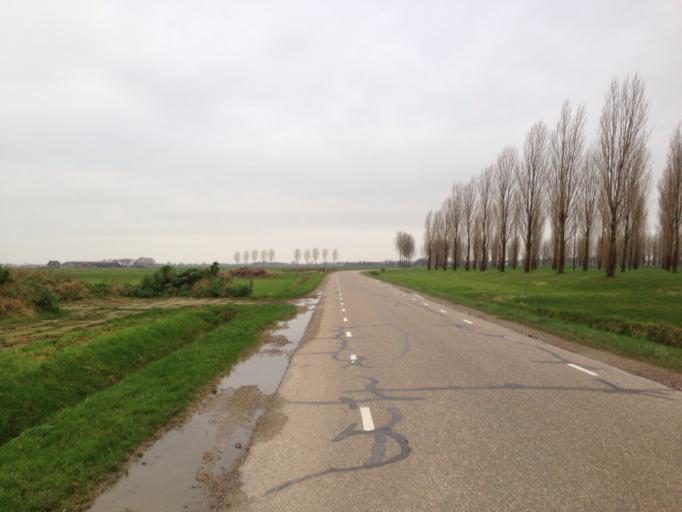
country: NL
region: Gelderland
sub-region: Gemeente Maasdriel
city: Hedel
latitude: 51.7240
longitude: 5.2388
